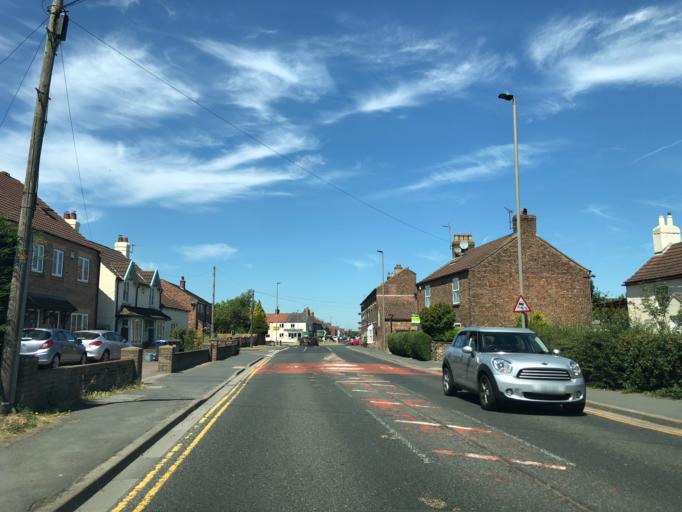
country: GB
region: England
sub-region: North Yorkshire
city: Thirsk
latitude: 54.2325
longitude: -1.3352
